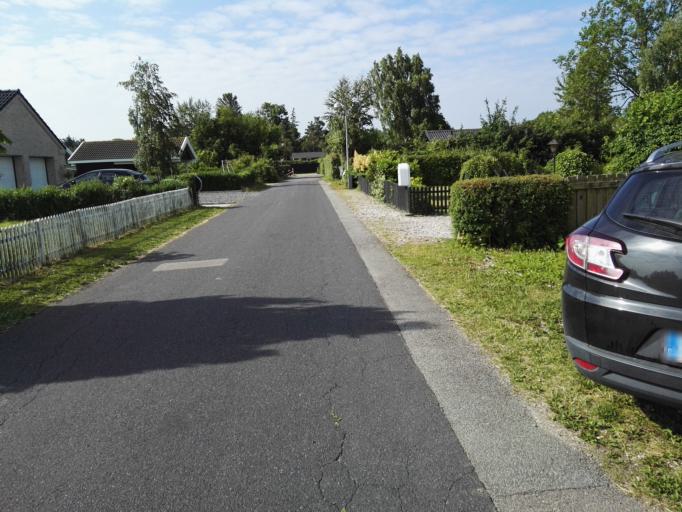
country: DK
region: Zealand
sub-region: Roskilde Kommune
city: Jyllinge
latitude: 55.7695
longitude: 12.1062
